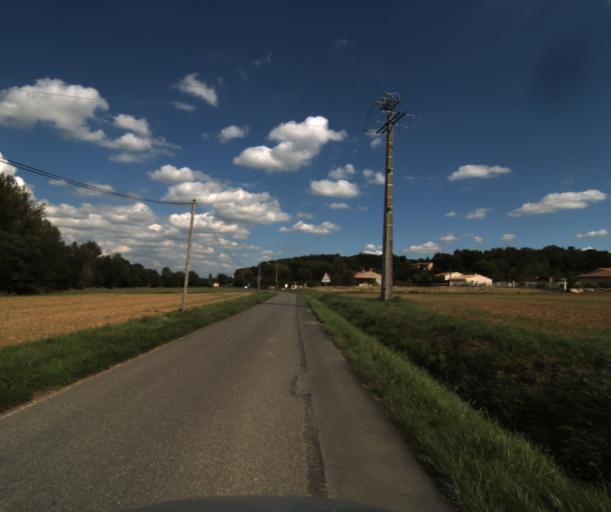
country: FR
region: Midi-Pyrenees
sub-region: Departement de la Haute-Garonne
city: Eaunes
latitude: 43.4164
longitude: 1.3586
